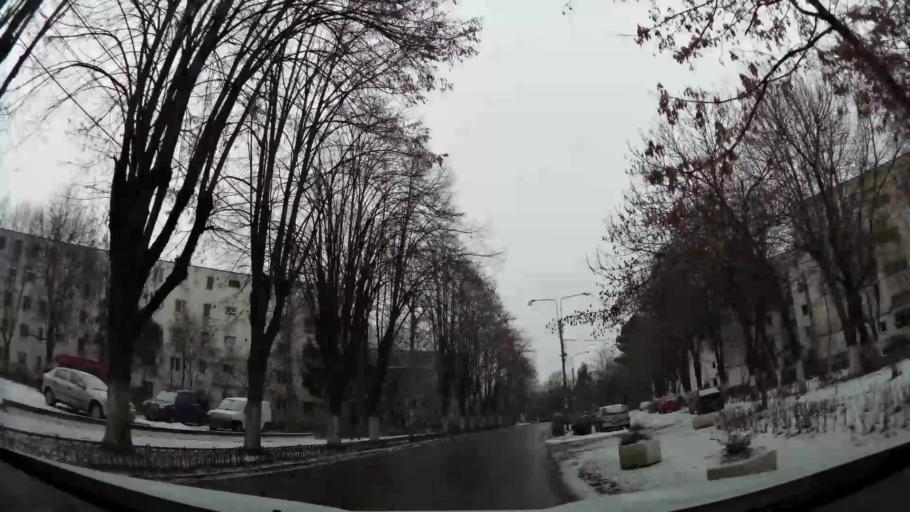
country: RO
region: Prahova
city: Ploiesti
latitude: 44.9605
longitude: 26.0026
